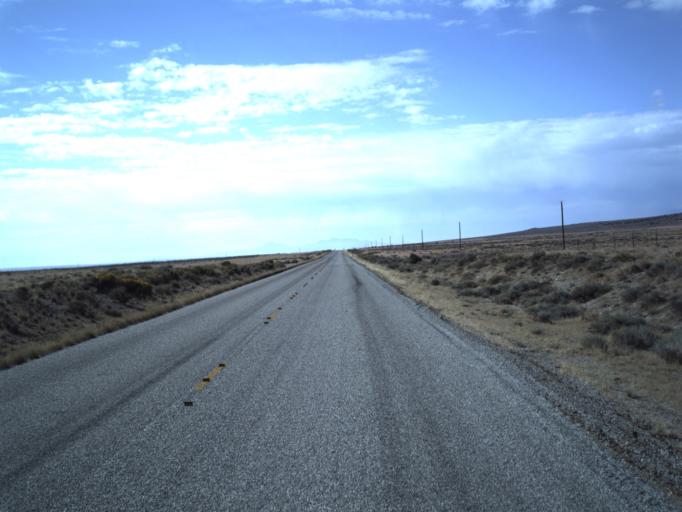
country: US
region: Utah
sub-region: Tooele County
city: Wendover
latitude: 41.5498
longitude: -113.5871
